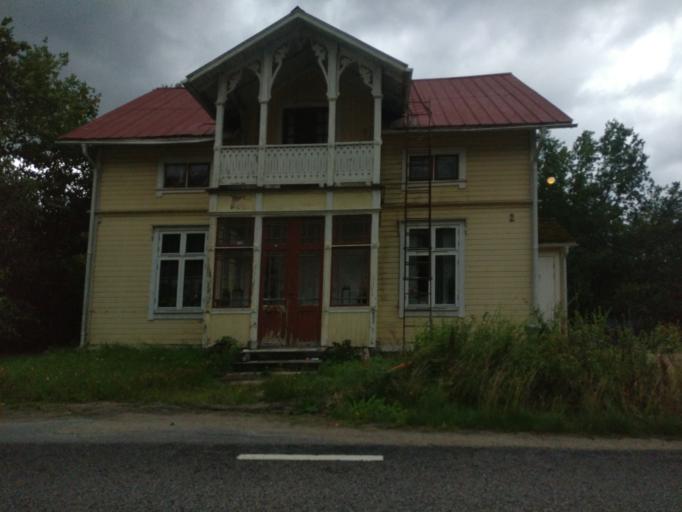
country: SE
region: Vaermland
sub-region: Torsby Kommun
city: Torsby
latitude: 60.7305
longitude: 12.8709
